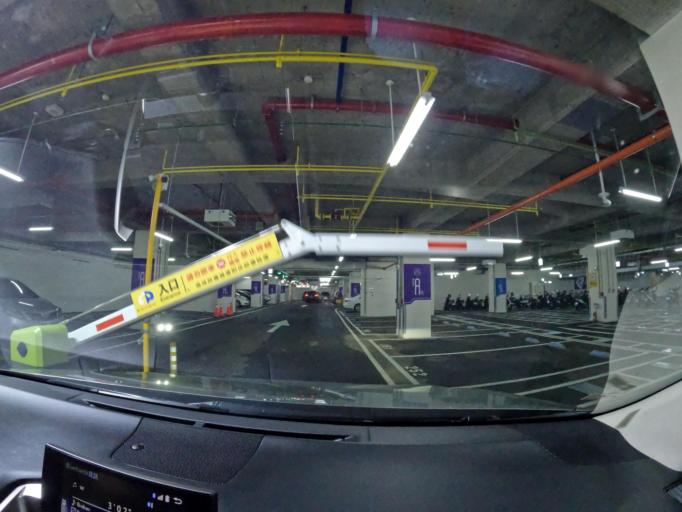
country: TW
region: Kaohsiung
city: Kaohsiung
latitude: 22.7801
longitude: 120.2997
